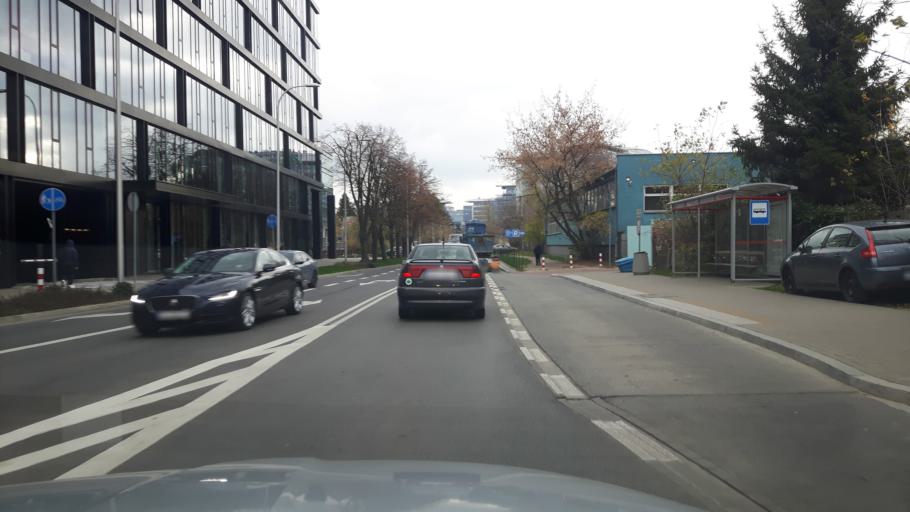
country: PL
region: Masovian Voivodeship
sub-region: Warszawa
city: Ochota
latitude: 52.1851
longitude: 20.9885
